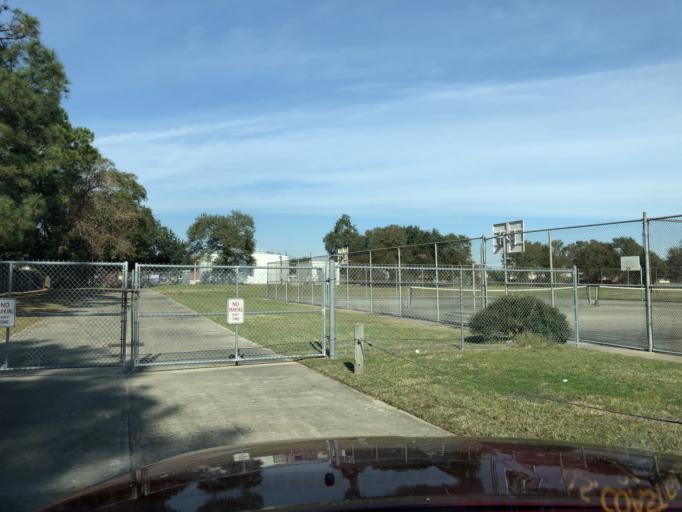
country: US
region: Texas
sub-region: Harris County
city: Tomball
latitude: 30.0308
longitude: -95.5513
